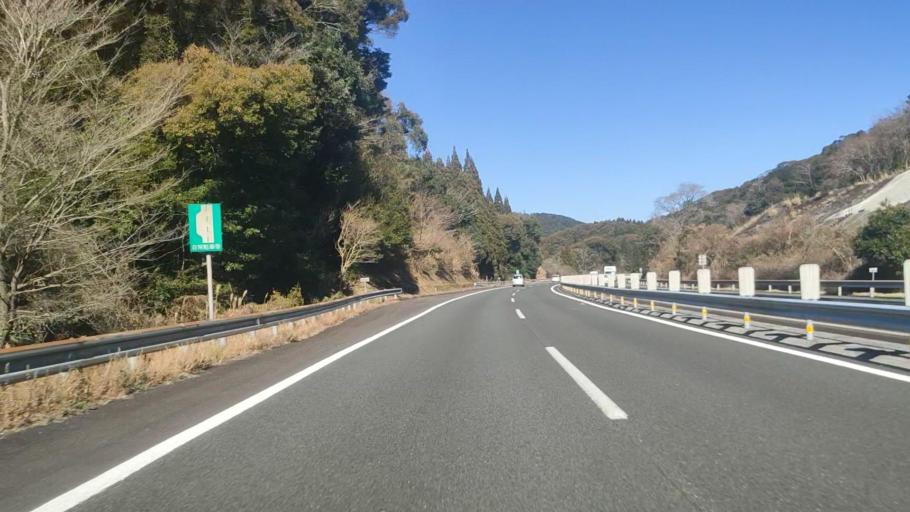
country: JP
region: Miyazaki
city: Miyakonojo
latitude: 31.8169
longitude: 131.2162
